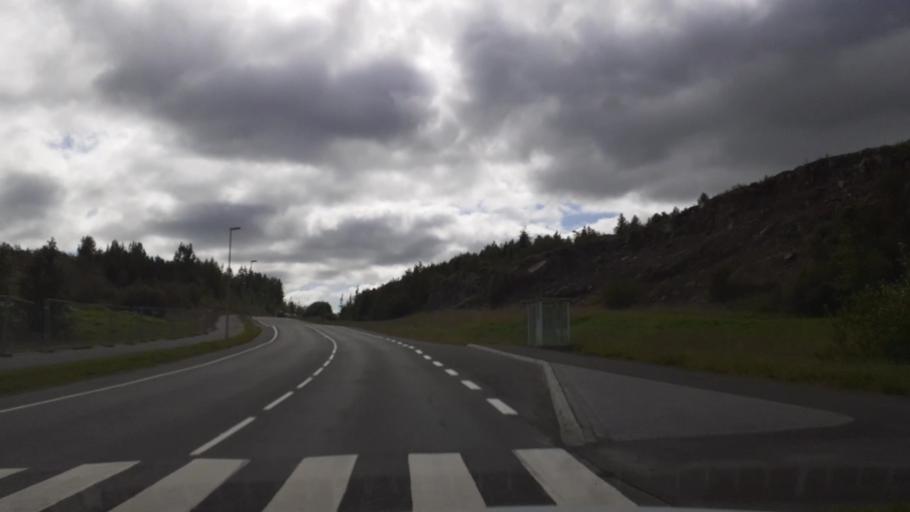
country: IS
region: Northeast
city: Akureyri
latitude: 65.6846
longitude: -18.1157
